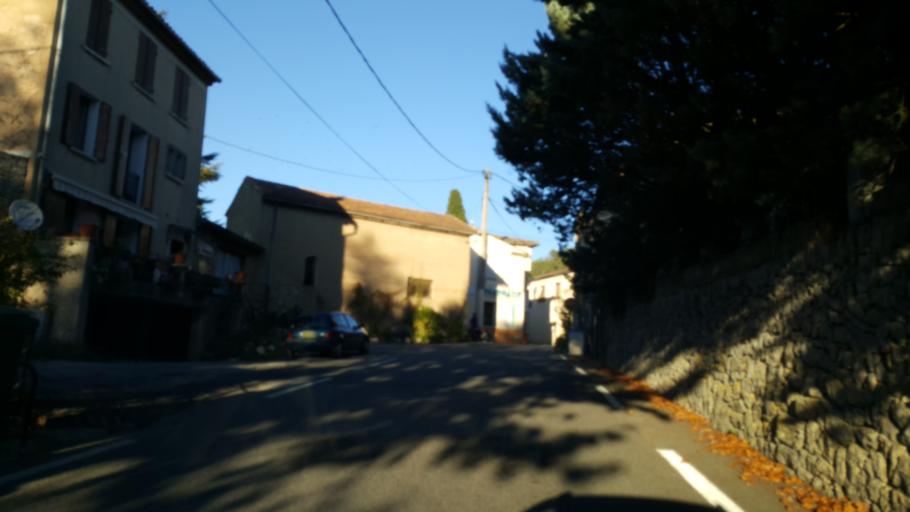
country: FR
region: Provence-Alpes-Cote d'Azur
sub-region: Departement du Var
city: Barjols
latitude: 43.5976
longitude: 5.9577
